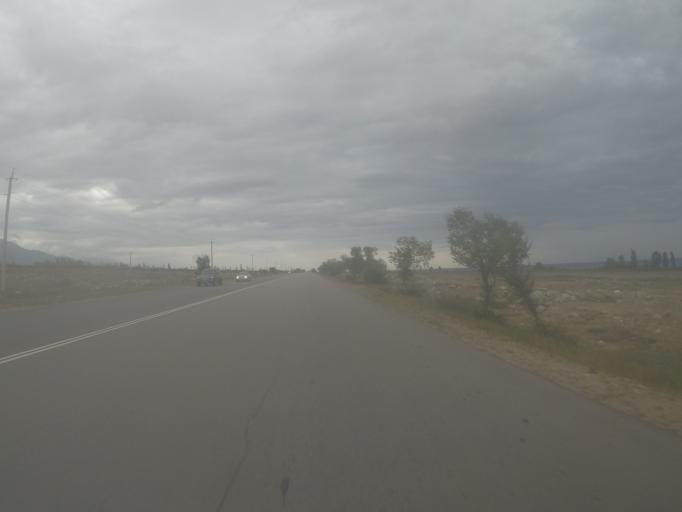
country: KG
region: Ysyk-Koel
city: Cholpon-Ata
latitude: 42.5973
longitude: 76.8168
